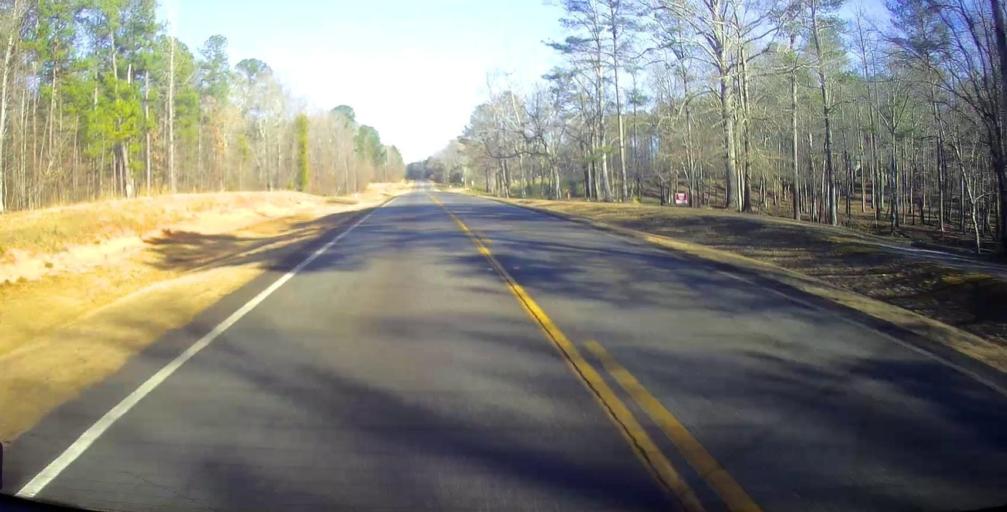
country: US
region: Georgia
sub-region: Talbot County
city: Sardis
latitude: 32.7782
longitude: -84.6793
